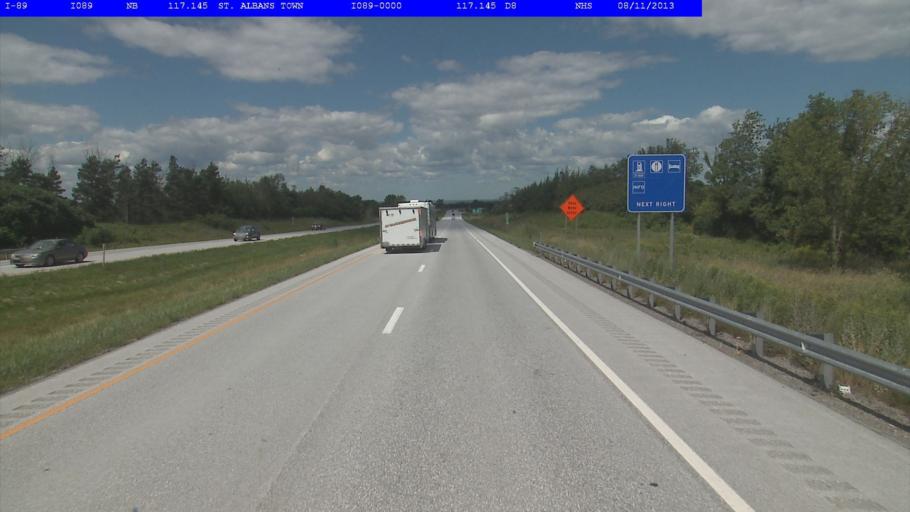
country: US
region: Vermont
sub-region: Franklin County
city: Saint Albans
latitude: 44.8402
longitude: -73.0711
